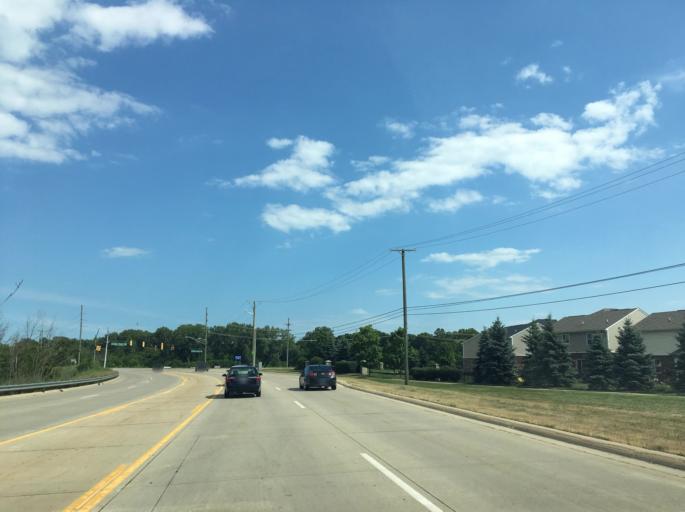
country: US
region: Michigan
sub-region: Macomb County
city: Clinton
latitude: 42.6037
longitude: -82.9153
